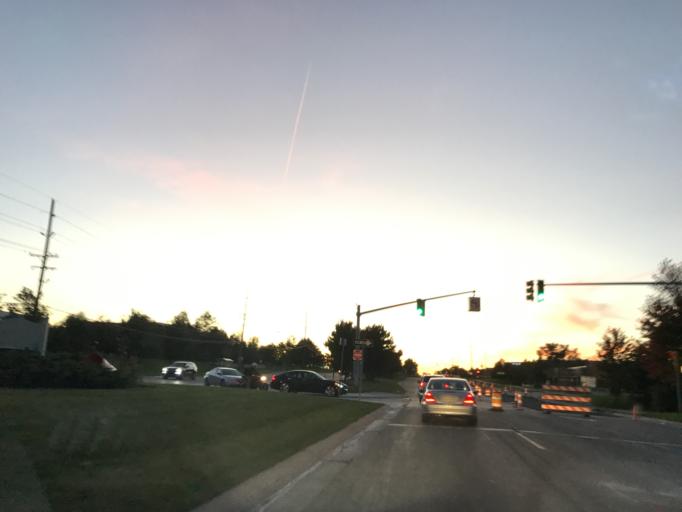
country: US
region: Michigan
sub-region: Oakland County
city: Novi
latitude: 42.4972
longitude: -83.4329
